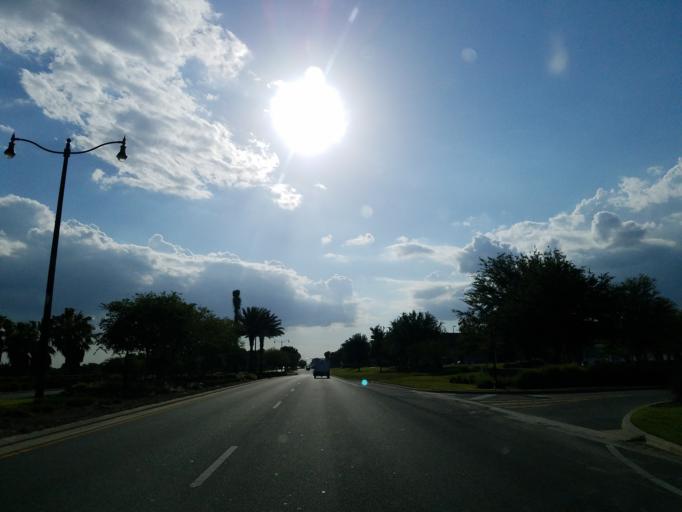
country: US
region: Florida
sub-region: Lake County
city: Fruitland Park
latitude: 28.8654
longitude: -81.9608
